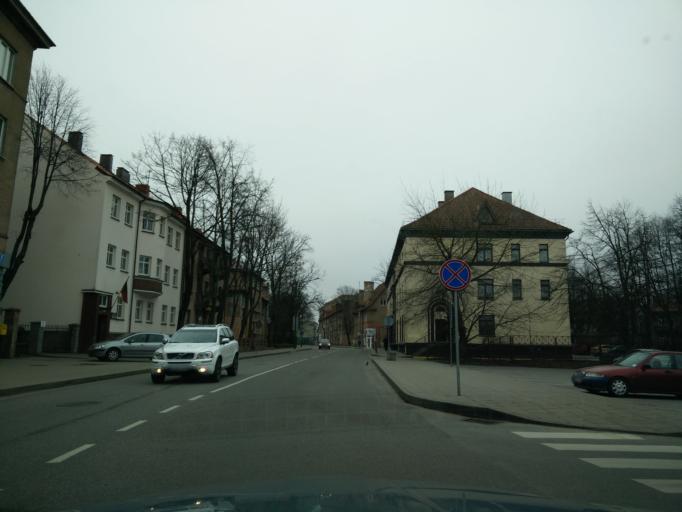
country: LT
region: Klaipedos apskritis
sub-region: Klaipeda
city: Klaipeda
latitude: 55.7050
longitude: 21.1380
